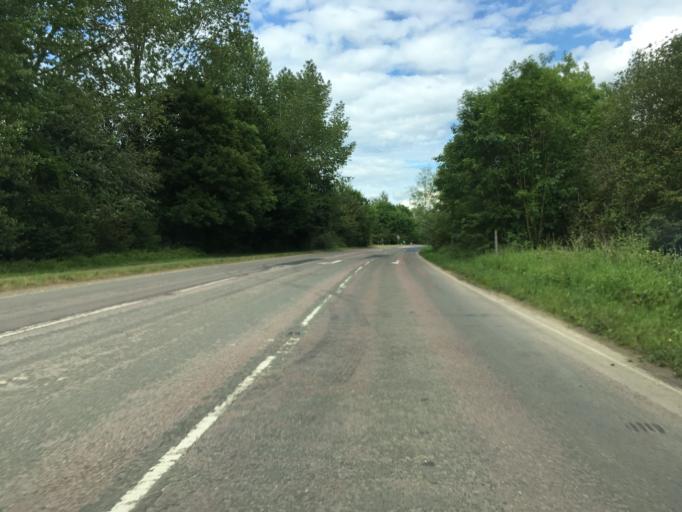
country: GB
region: England
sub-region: Wiltshire
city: Minety
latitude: 51.6540
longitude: -1.9630
